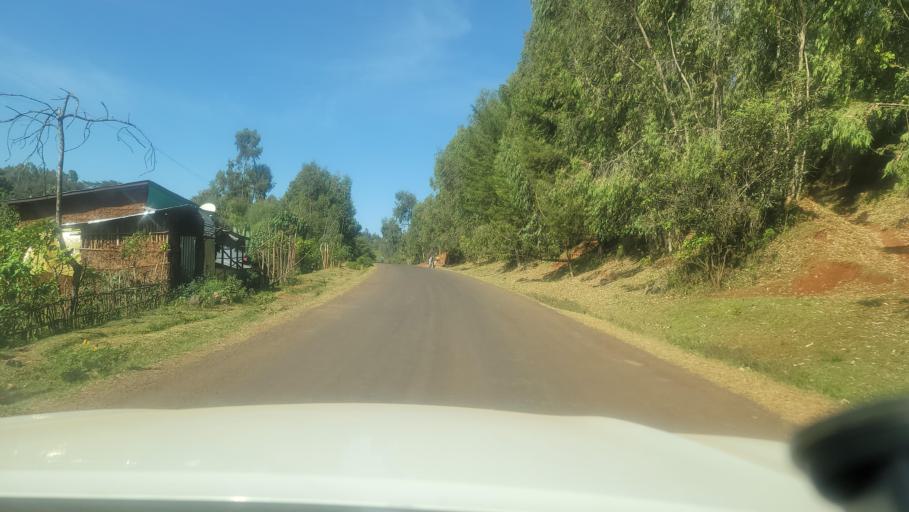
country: ET
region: Oromiya
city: Agaro
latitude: 7.7997
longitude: 36.4751
